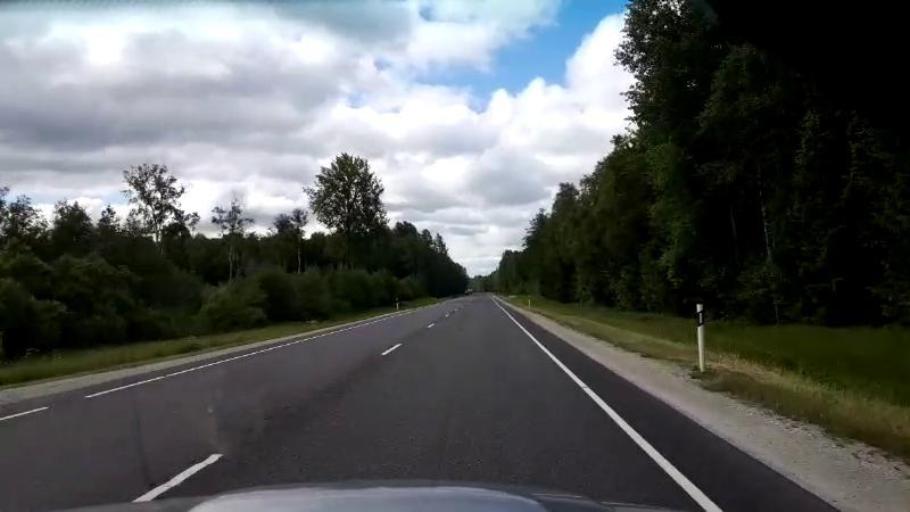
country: EE
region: Raplamaa
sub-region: Maerjamaa vald
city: Marjamaa
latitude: 58.8307
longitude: 24.4179
